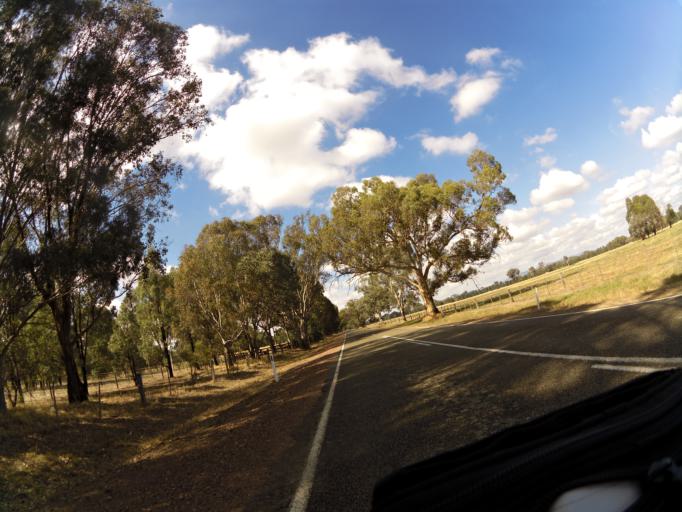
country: AU
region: Victoria
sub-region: Benalla
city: Benalla
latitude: -36.5859
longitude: 146.0082
